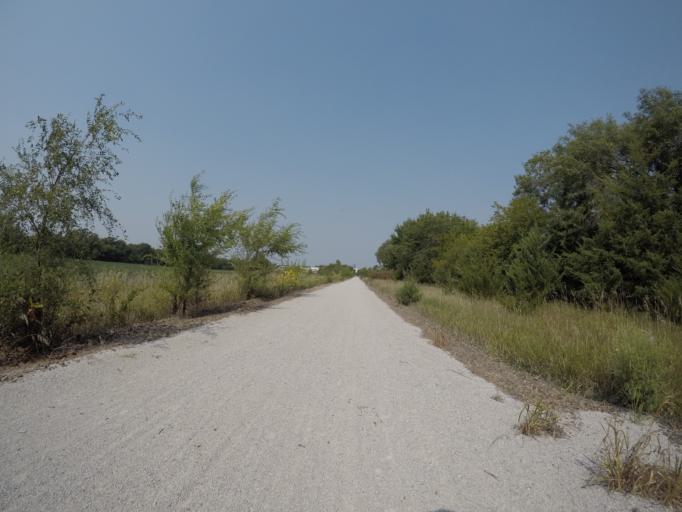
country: US
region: Nebraska
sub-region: Gage County
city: Beatrice
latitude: 40.2561
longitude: -96.7373
